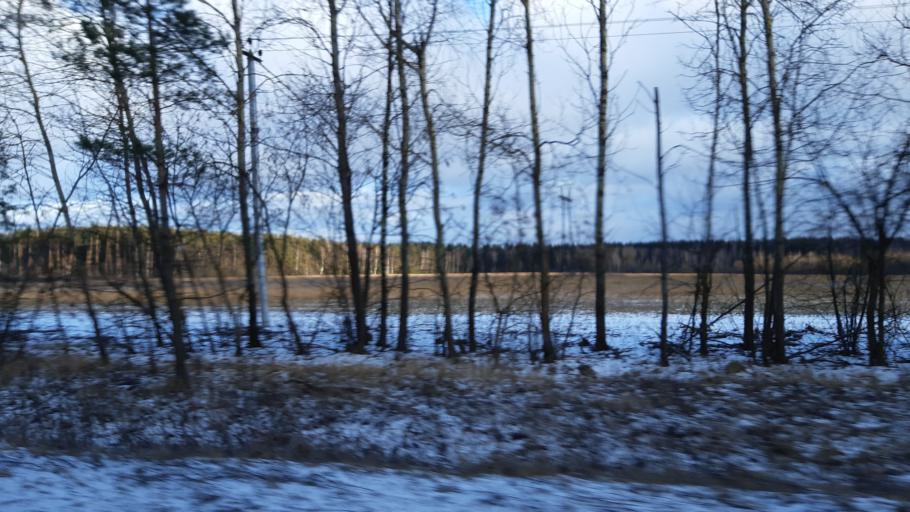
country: RU
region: Moskovskaya
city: Noginsk-9
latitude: 56.0432
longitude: 38.5525
